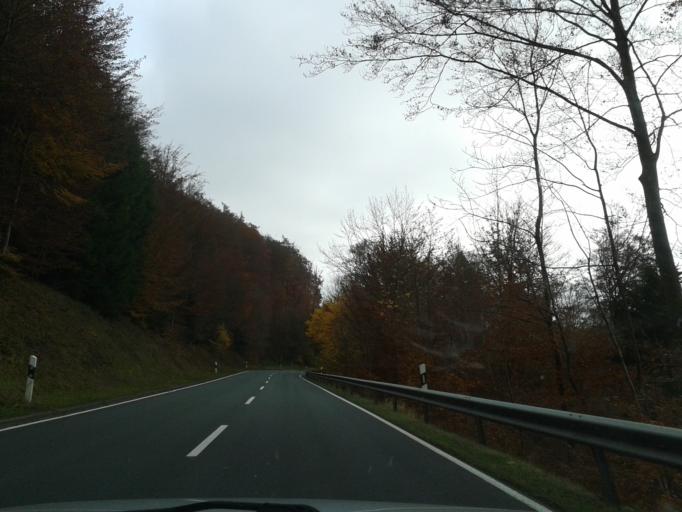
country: DE
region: North Rhine-Westphalia
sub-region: Regierungsbezirk Arnsberg
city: Erndtebruck
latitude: 50.9735
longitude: 8.3384
